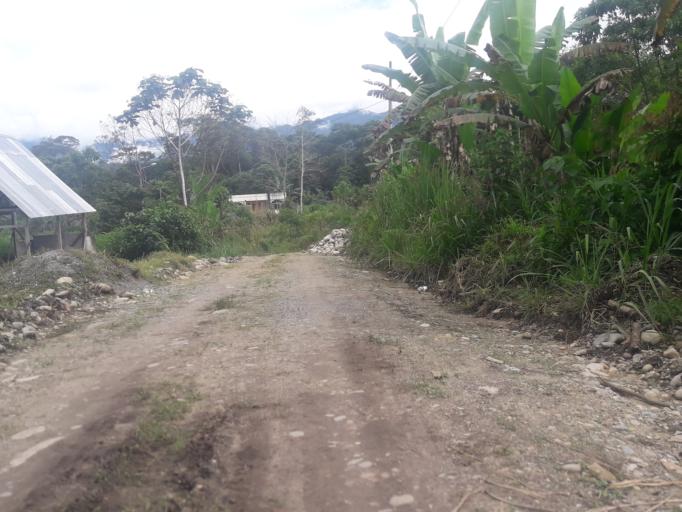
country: EC
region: Napo
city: Tena
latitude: -0.9745
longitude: -77.8440
